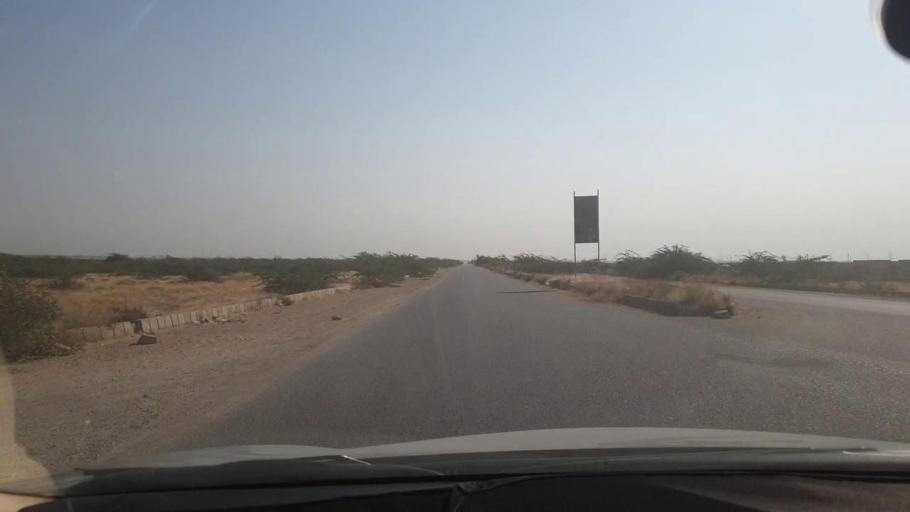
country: PK
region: Sindh
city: Malir Cantonment
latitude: 25.0721
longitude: 67.1386
